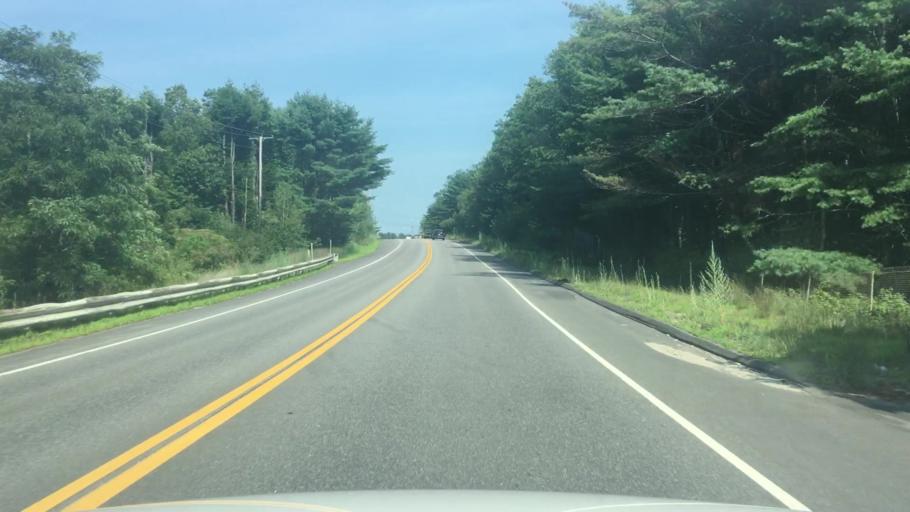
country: US
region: Maine
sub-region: Cumberland County
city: Brunswick
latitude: 43.9065
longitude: -69.9286
